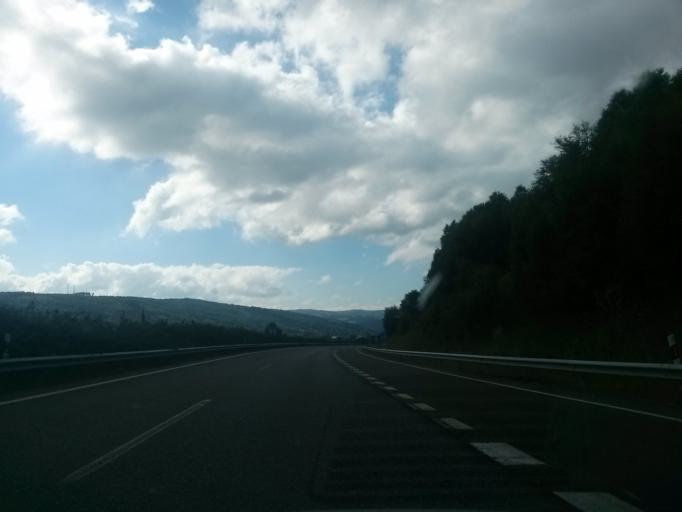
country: ES
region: Galicia
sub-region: Provincia de Lugo
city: Becerrea
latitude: 42.8879
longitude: -7.1804
